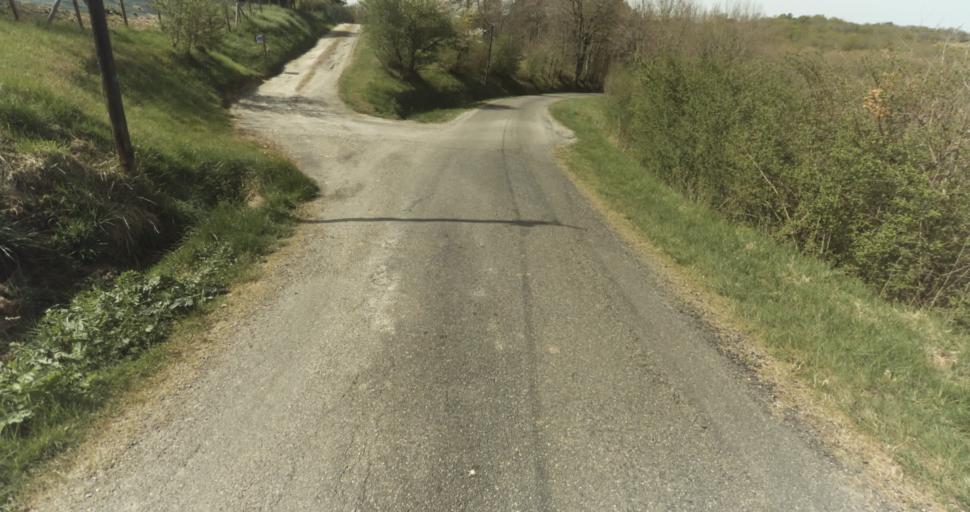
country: FR
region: Midi-Pyrenees
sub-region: Departement du Tarn-et-Garonne
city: Moissac
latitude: 44.1611
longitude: 1.1187
